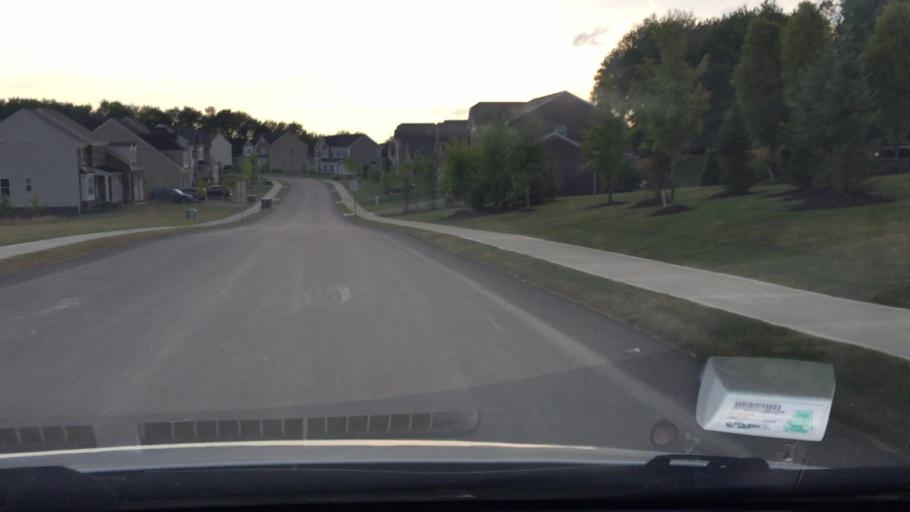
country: US
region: Pennsylvania
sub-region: Allegheny County
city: Gibsonia
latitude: 40.6395
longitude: -80.0220
